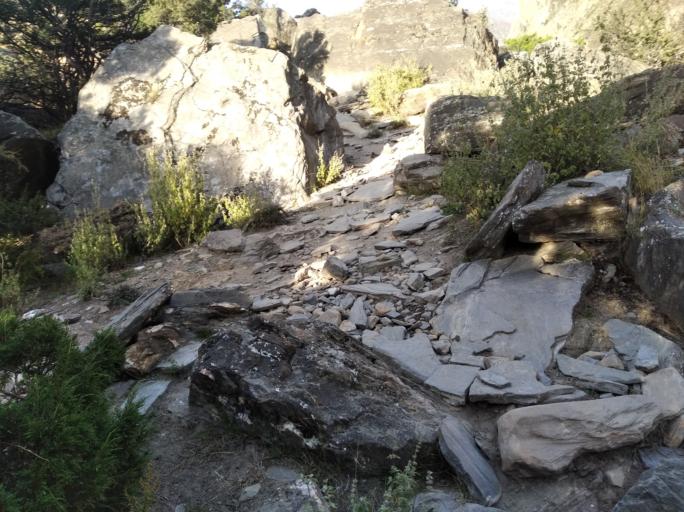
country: NP
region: Western Region
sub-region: Dhawalagiri Zone
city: Jomsom
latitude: 28.8822
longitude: 83.1598
